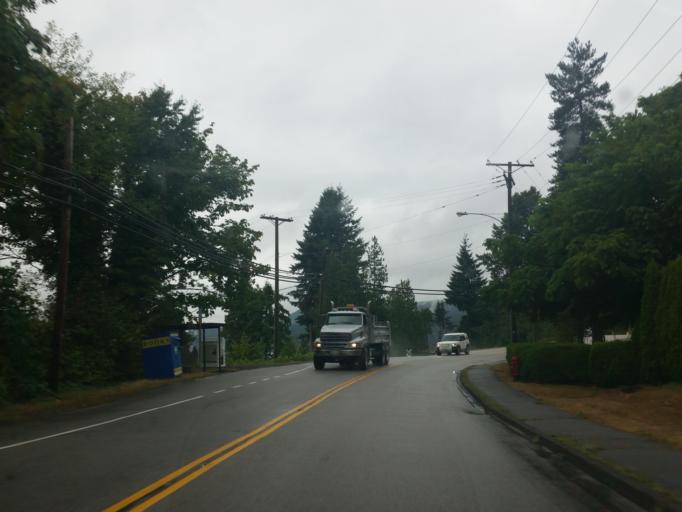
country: CA
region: British Columbia
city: Port Moody
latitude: 49.2924
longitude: -122.8524
